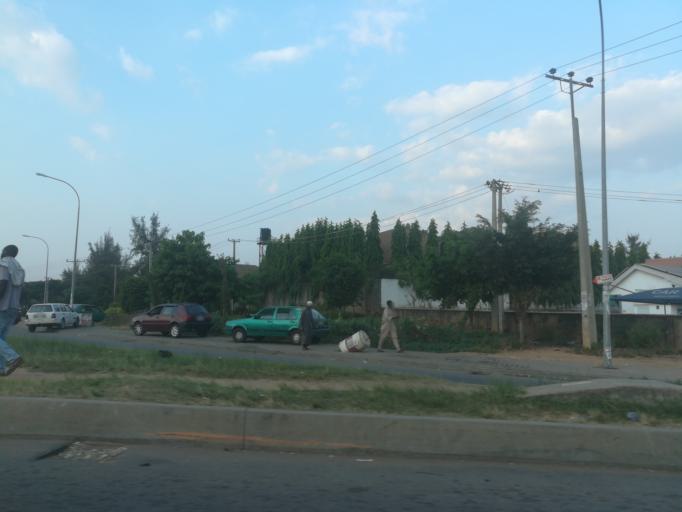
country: NG
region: Abuja Federal Capital Territory
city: Abuja
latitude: 9.0651
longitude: 7.4111
